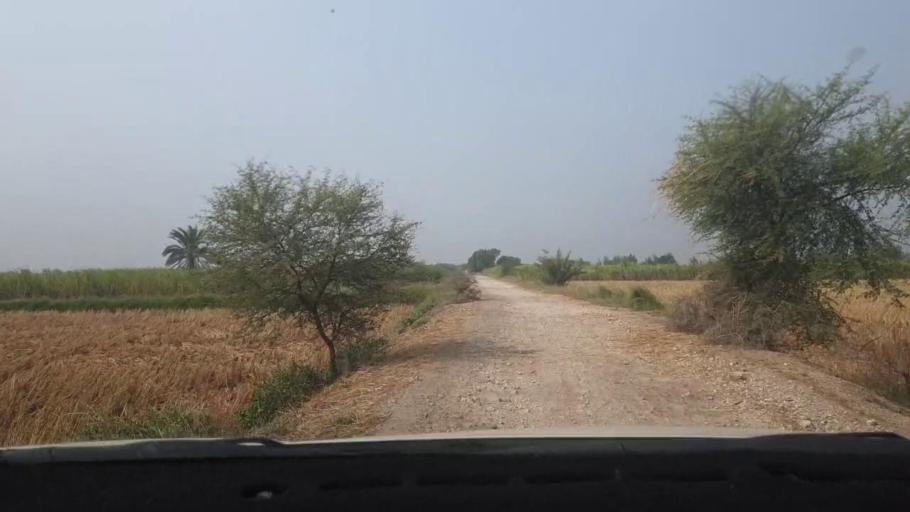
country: PK
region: Sindh
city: Tando Muhammad Khan
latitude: 25.0181
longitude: 68.5403
